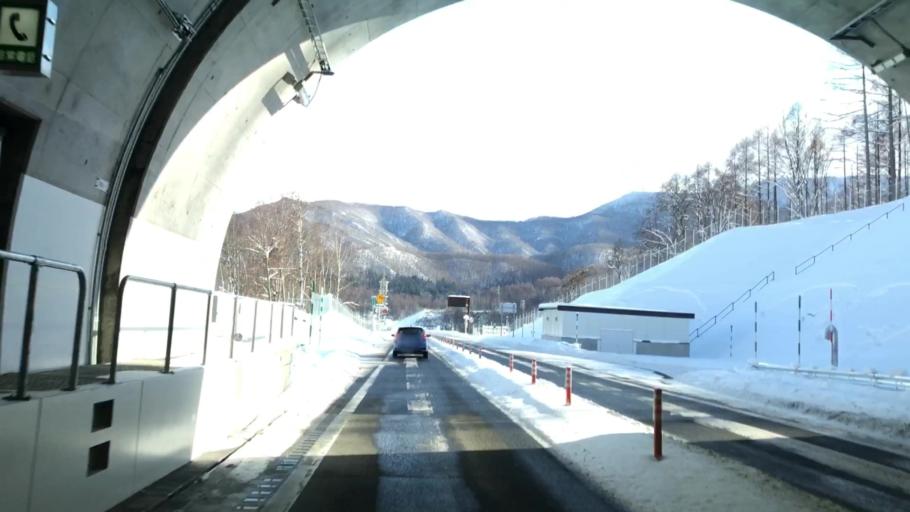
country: JP
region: Hokkaido
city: Otaru
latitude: 43.1740
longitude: 140.9768
